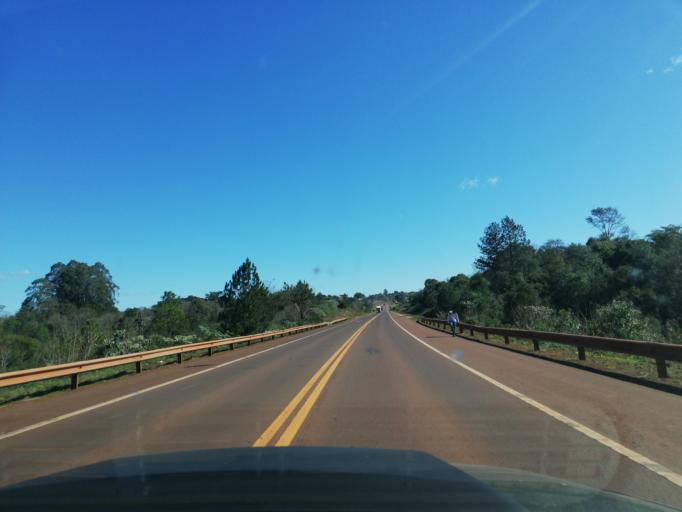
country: AR
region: Misiones
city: Aristobulo del Valle
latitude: -27.0986
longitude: -54.8766
